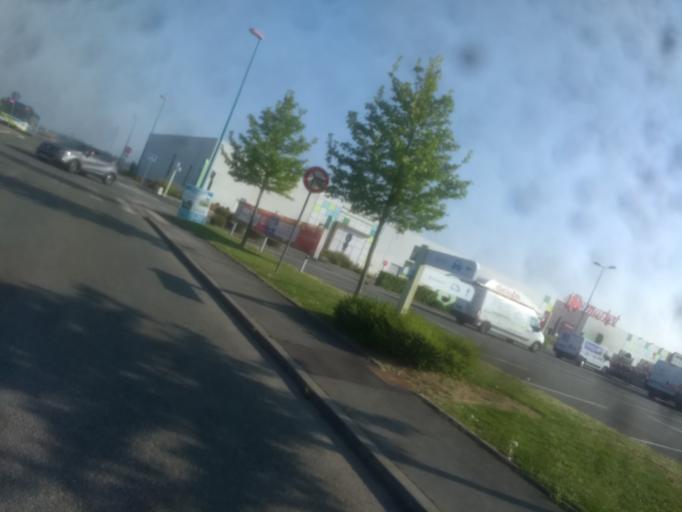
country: FR
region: Nord-Pas-de-Calais
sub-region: Departement du Pas-de-Calais
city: Beaurains
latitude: 50.2636
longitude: 2.7985
